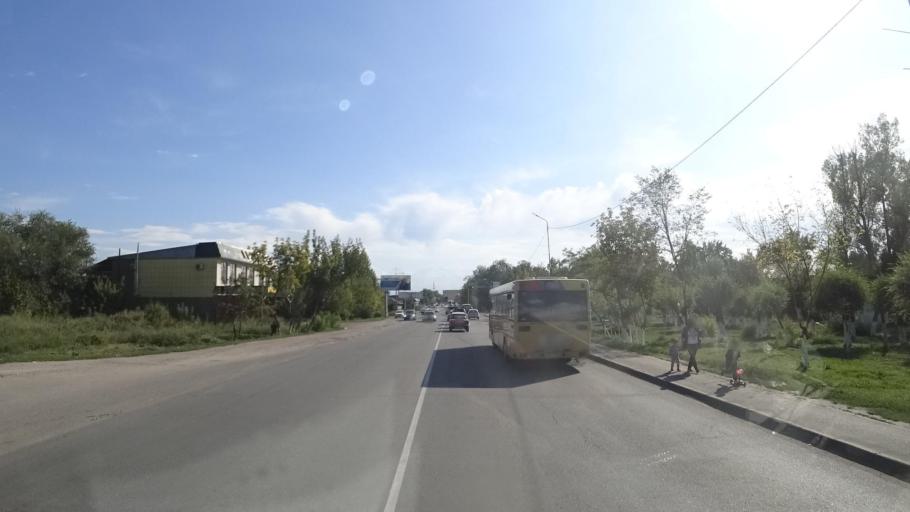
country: KZ
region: Almaty Oblysy
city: Energeticheskiy
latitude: 43.4148
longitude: 77.0205
